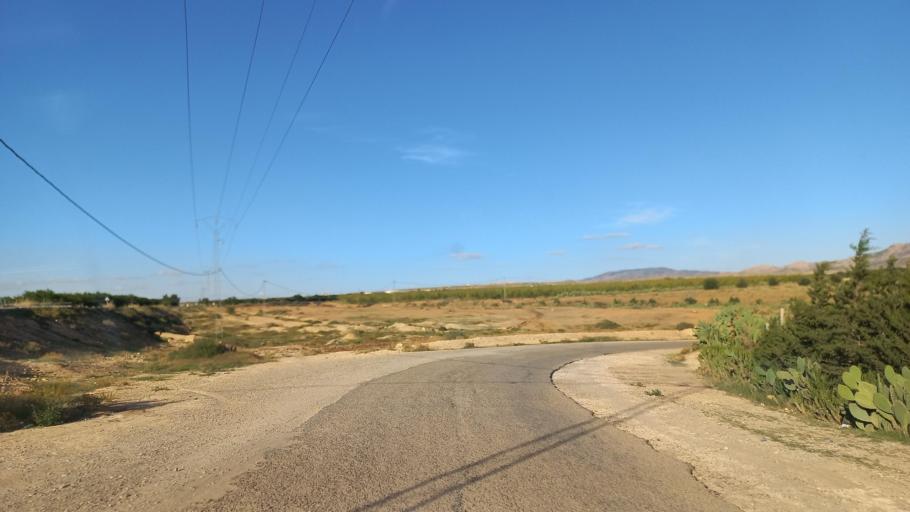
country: TN
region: Al Qasrayn
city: Sbiba
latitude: 35.3347
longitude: 9.0875
